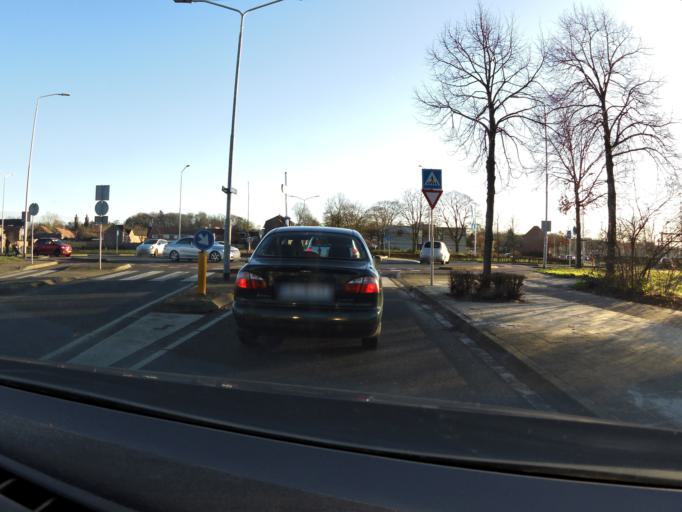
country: NL
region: Limburg
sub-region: Gemeente Venlo
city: Venlo
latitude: 51.3594
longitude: 6.1779
